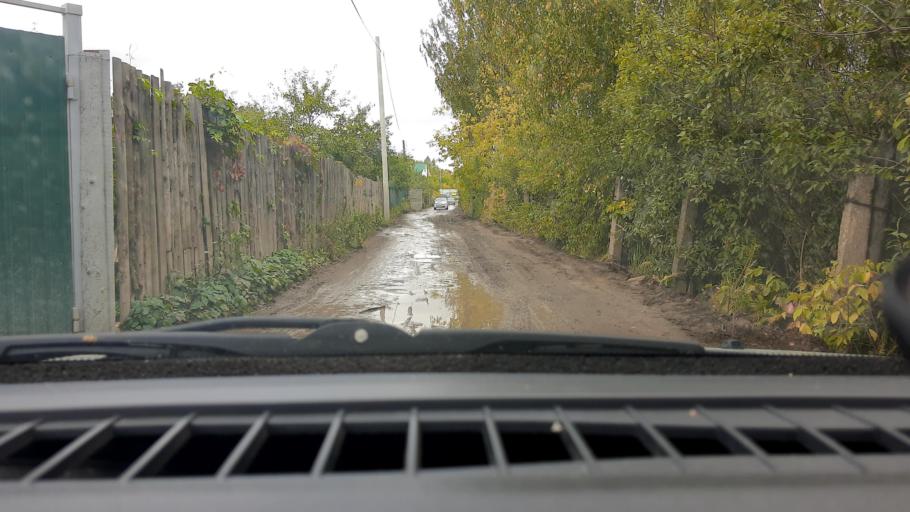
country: RU
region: Nizjnij Novgorod
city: Gorbatovka
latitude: 56.3236
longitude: 43.8385
